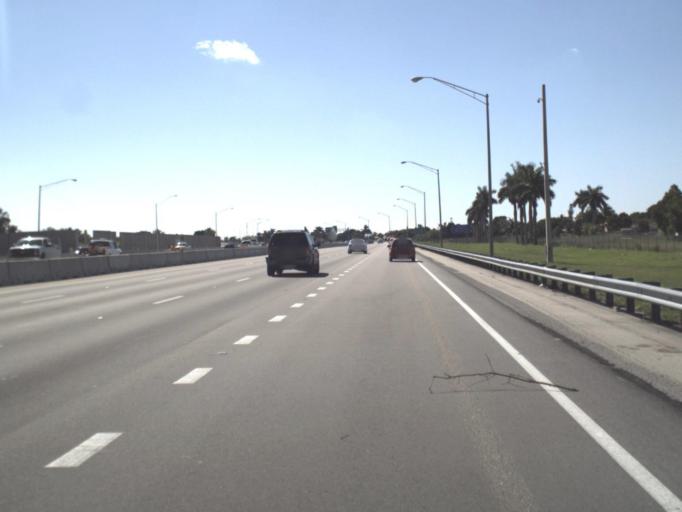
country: US
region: Florida
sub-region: Miami-Dade County
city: South Miami Heights
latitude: 25.6073
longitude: -80.3784
